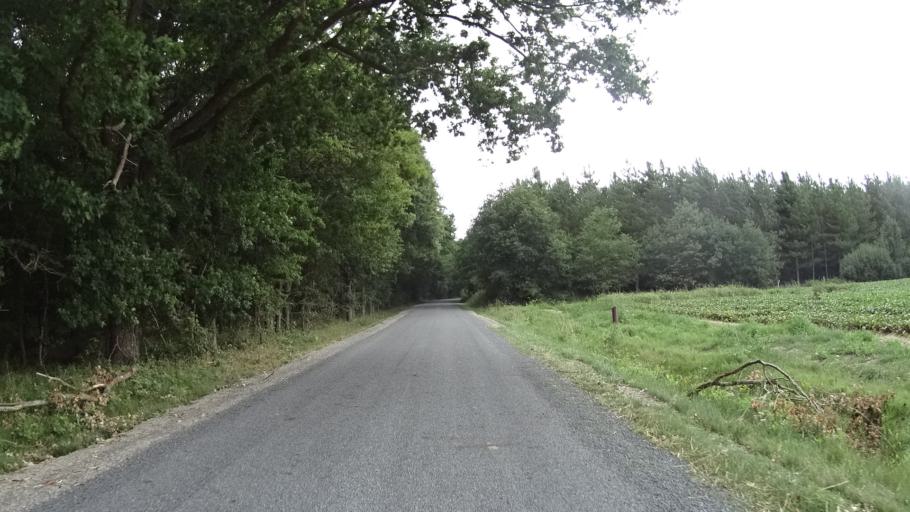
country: FR
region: Centre
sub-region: Departement du Loiret
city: Chevillon-sur-Huillard
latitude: 47.9415
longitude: 2.5727
